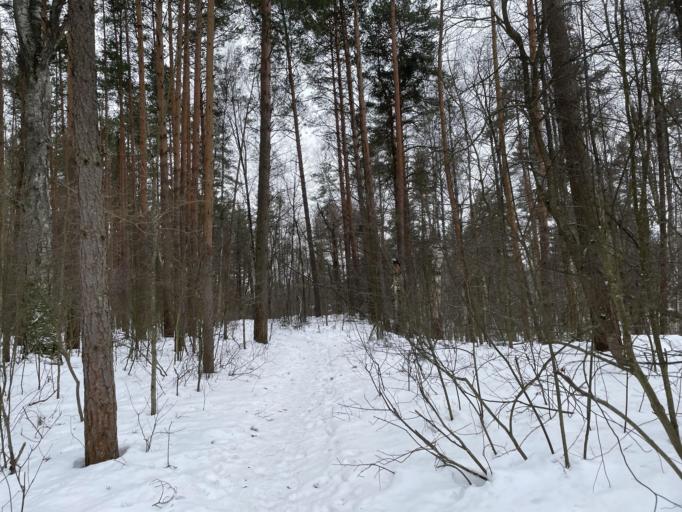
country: RU
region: Vladimir
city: Pokrov
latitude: 55.9403
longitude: 39.2372
